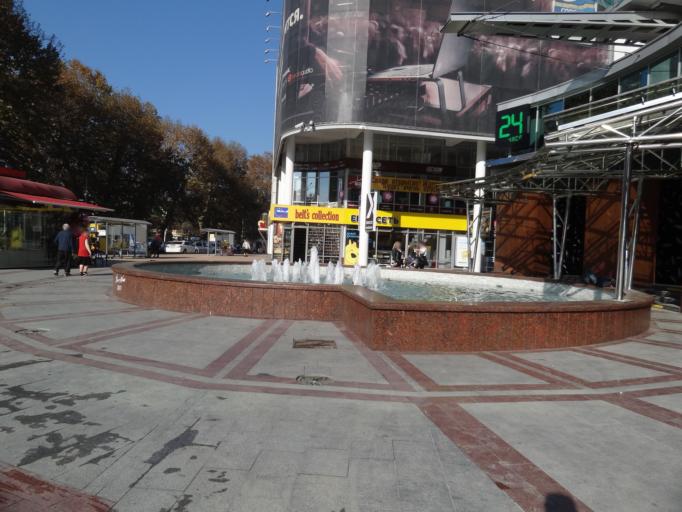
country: RU
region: Krasnodarskiy
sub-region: Sochi City
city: Sochi
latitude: 43.5840
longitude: 39.7205
